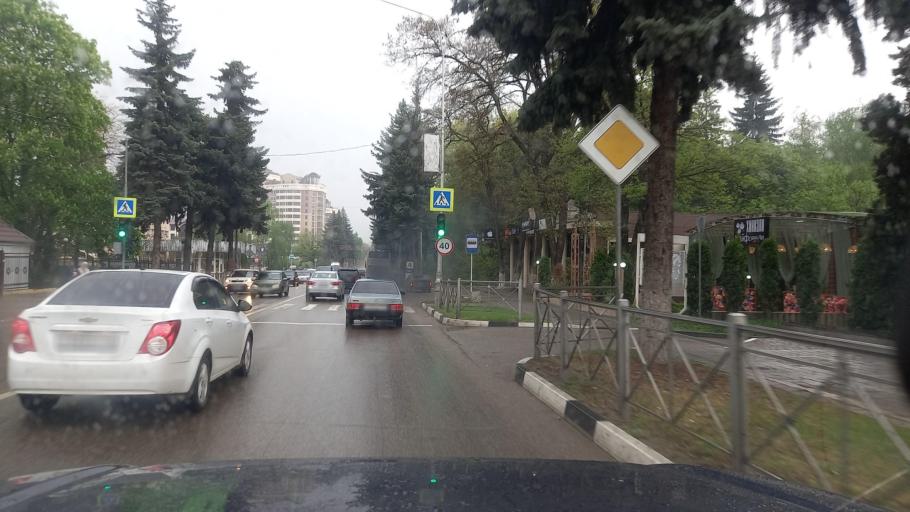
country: RU
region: Stavropol'skiy
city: Kislovodsk
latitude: 43.9144
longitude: 42.7194
